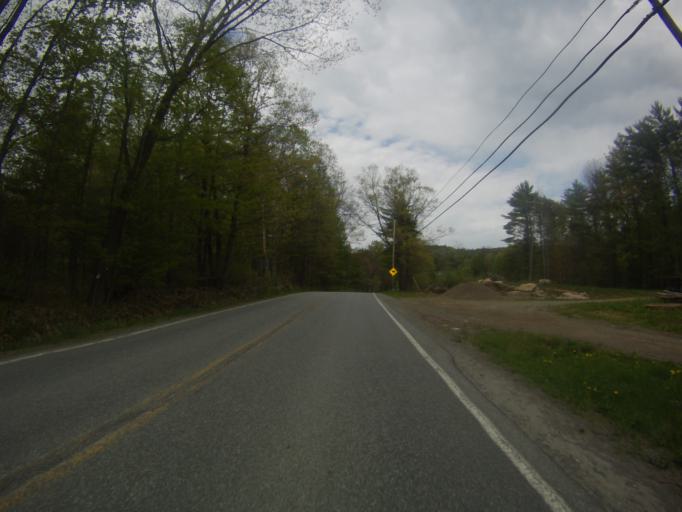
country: US
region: New York
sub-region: Essex County
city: Port Henry
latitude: 43.9664
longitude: -73.4893
